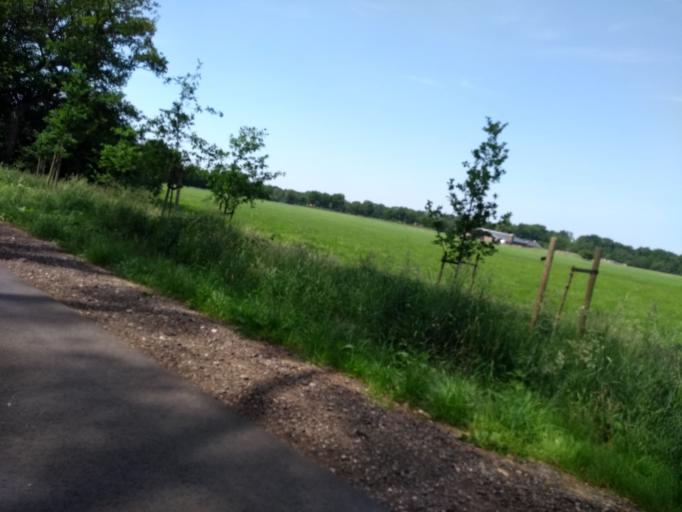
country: NL
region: Overijssel
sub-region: Gemeente Almelo
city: Almelo
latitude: 52.3629
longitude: 6.6993
